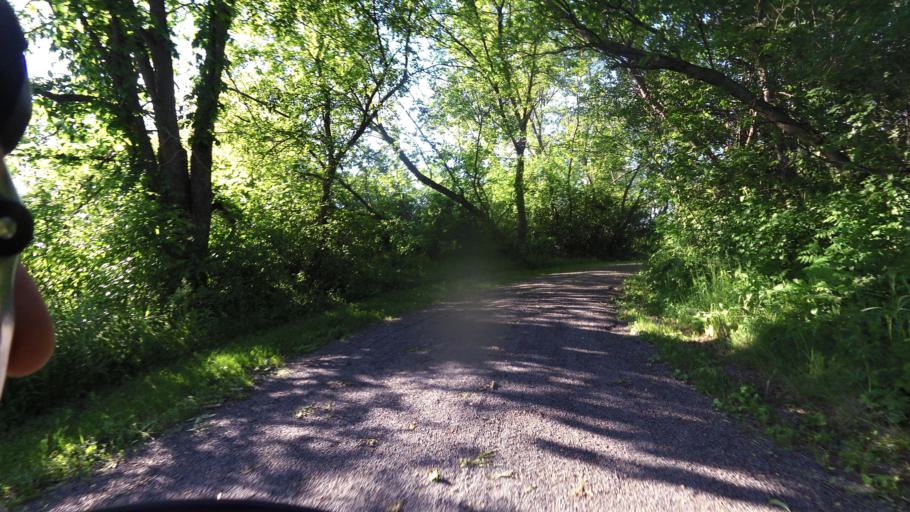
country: CA
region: Ontario
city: Bells Corners
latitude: 45.3422
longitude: -75.8712
